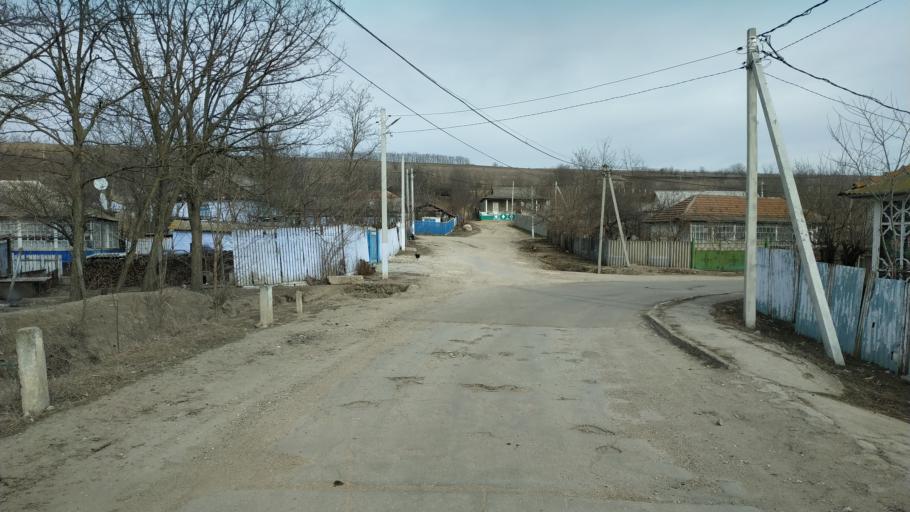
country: RO
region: Vaslui
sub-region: Comuna Dranceni
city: Dranceni
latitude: 46.8742
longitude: 28.2055
